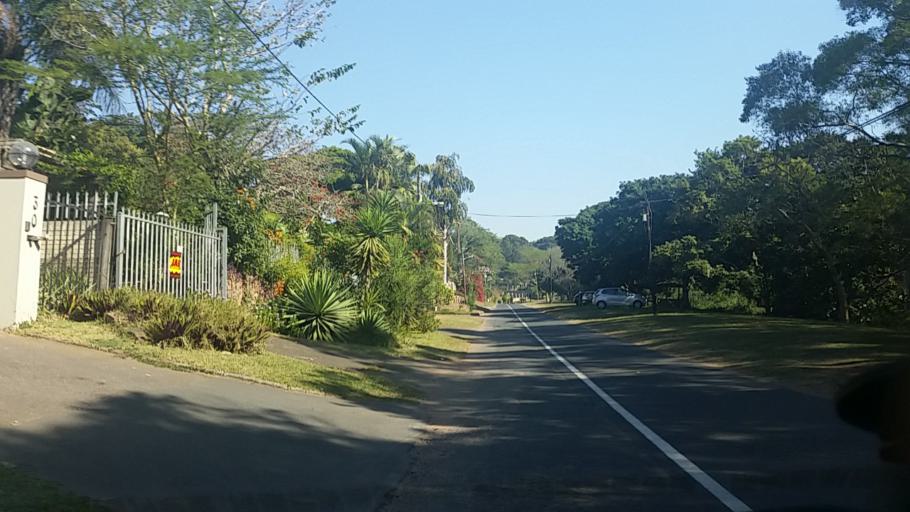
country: ZA
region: KwaZulu-Natal
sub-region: eThekwini Metropolitan Municipality
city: Berea
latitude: -29.8414
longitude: 30.9127
